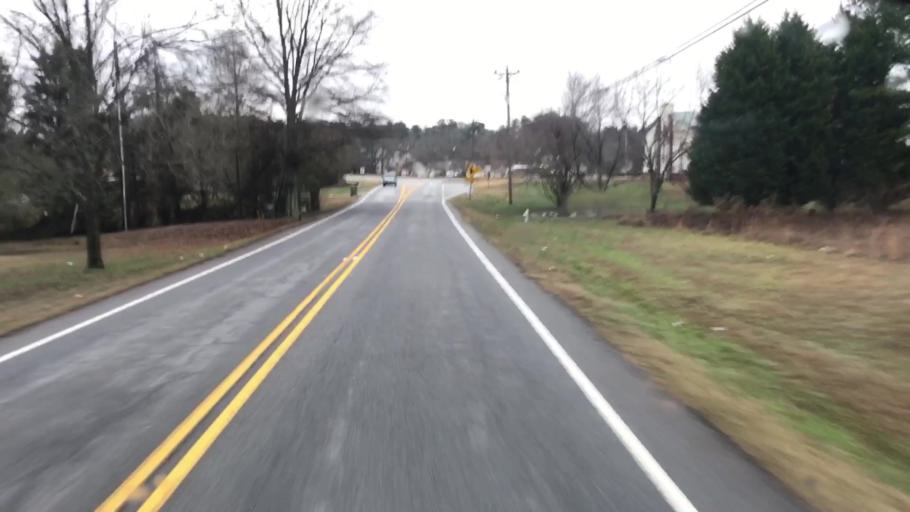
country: US
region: Georgia
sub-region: Walton County
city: Loganville
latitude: 33.8207
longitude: -83.9615
